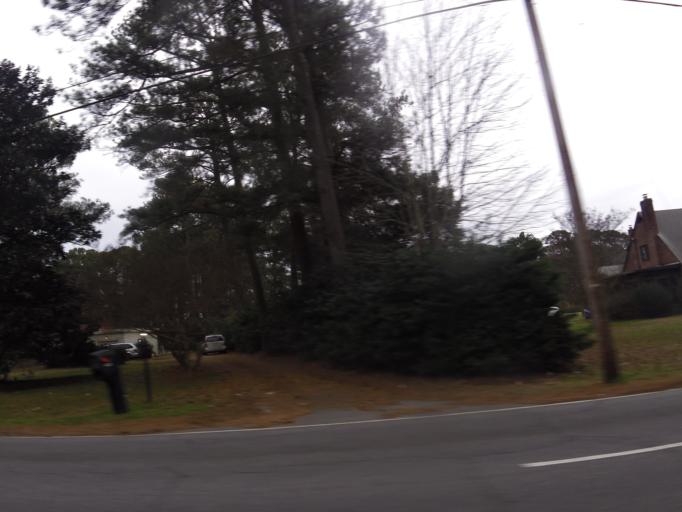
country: US
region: Virginia
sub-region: City of Portsmouth
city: Portsmouth Heights
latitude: 36.8497
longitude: -76.3761
